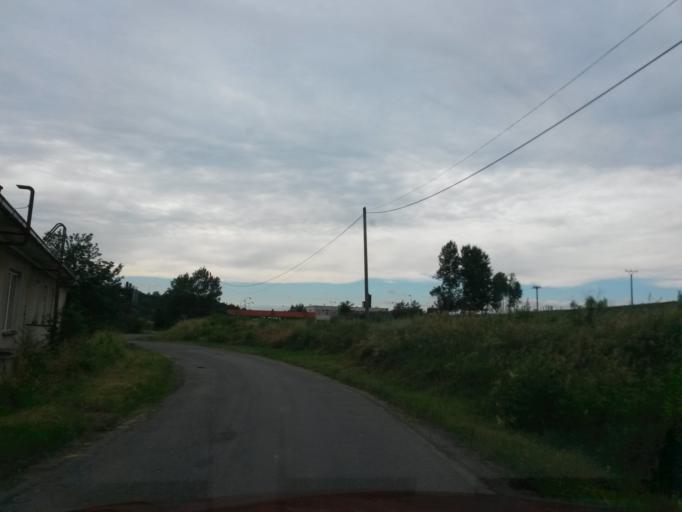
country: SK
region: Banskobystricky
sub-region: Okres Banska Bystrica
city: Zvolen
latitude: 48.5609
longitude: 19.2381
